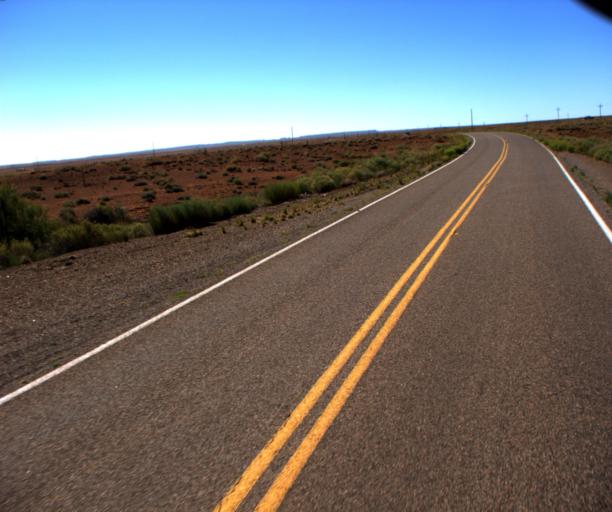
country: US
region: Arizona
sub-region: Coconino County
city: LeChee
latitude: 35.1906
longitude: -110.9384
